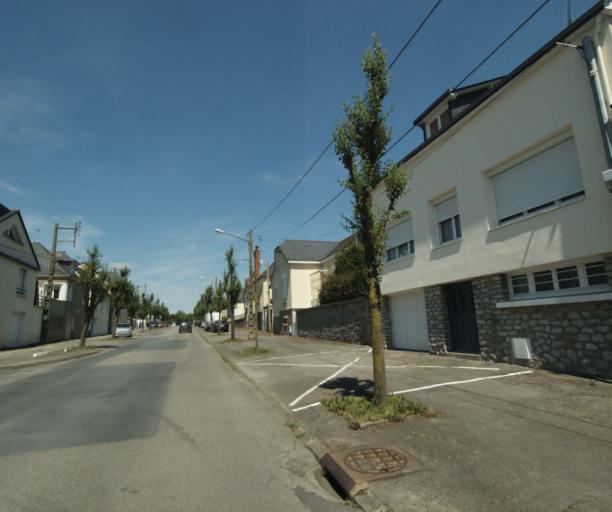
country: FR
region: Pays de la Loire
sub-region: Departement de la Mayenne
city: Laval
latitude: 48.0781
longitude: -0.7595
